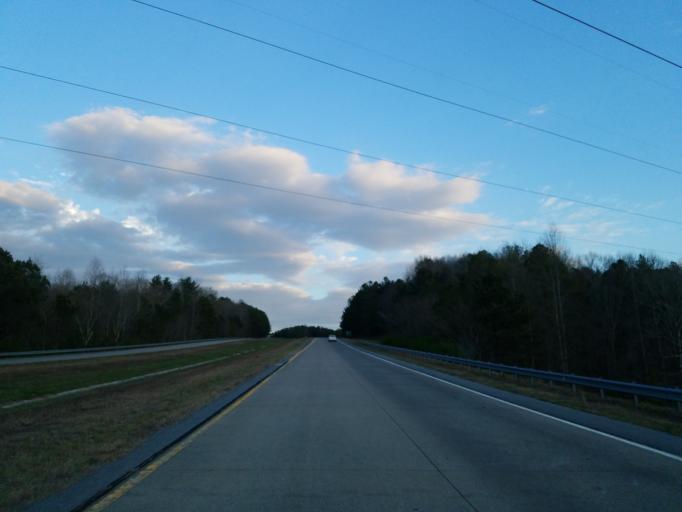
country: US
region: Georgia
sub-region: Pickens County
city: Nelson
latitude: 34.3739
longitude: -84.3814
